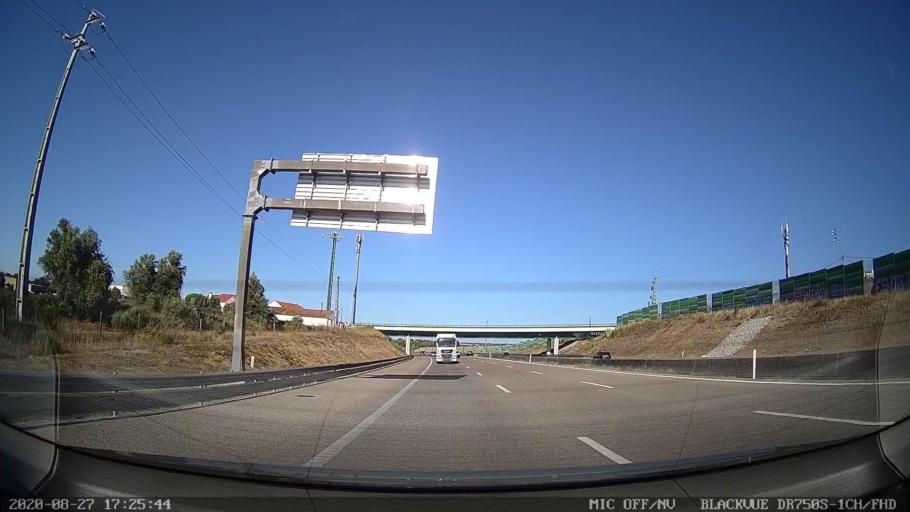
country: PT
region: Santarem
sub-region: Santarem
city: Santarem
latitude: 39.2782
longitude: -8.7015
